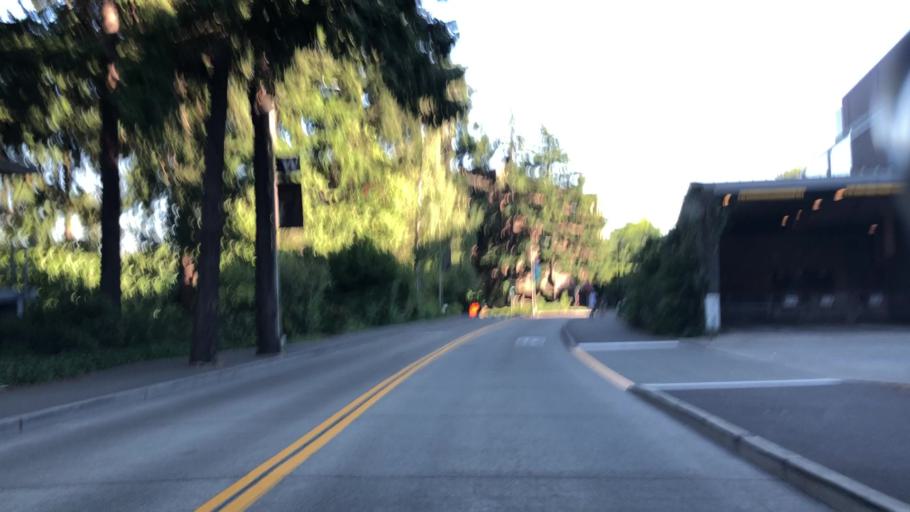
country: US
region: Washington
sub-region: King County
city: Seattle
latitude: 47.6558
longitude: -122.3045
